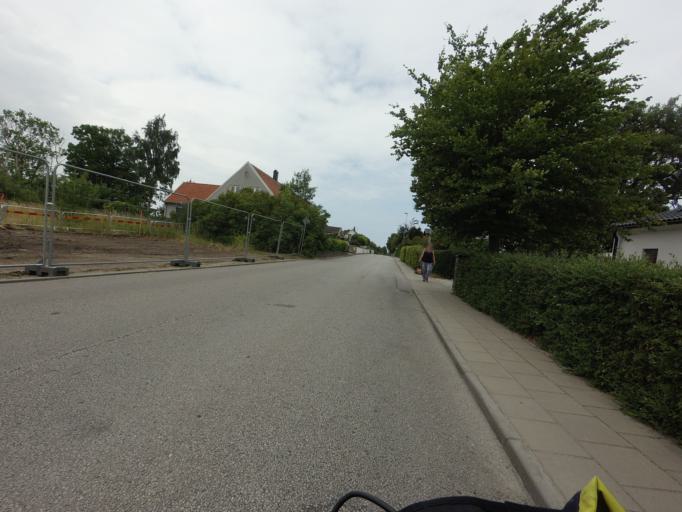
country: SE
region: Skane
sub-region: Malmo
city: Bunkeflostrand
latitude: 55.5299
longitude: 12.9349
